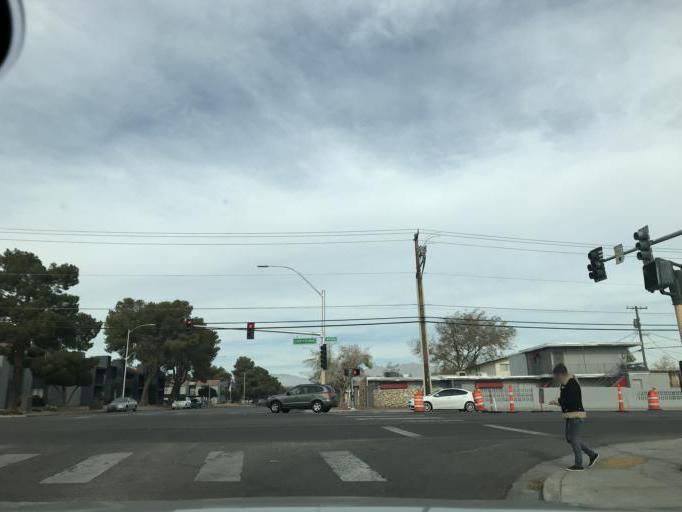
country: US
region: Nevada
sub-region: Clark County
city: Las Vegas
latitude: 36.2168
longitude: -115.2167
